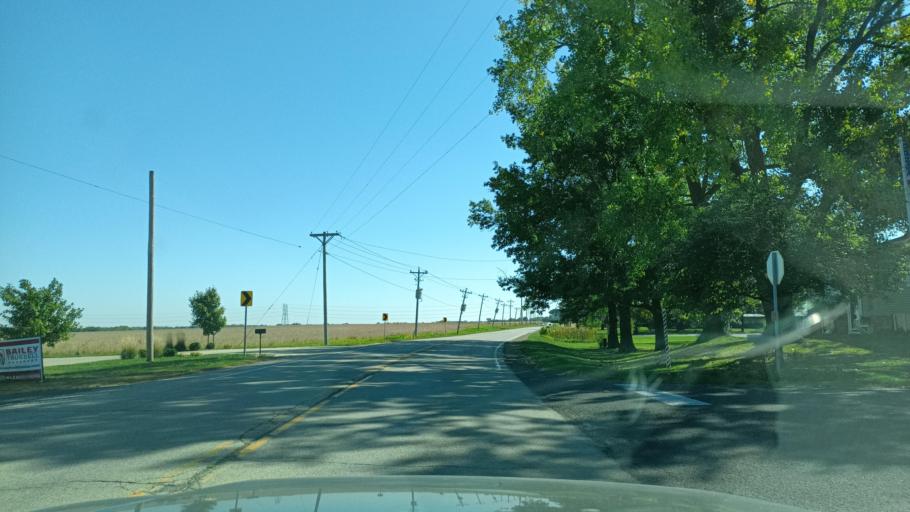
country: US
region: Illinois
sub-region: Peoria County
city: Dunlap
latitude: 40.7898
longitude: -89.7470
